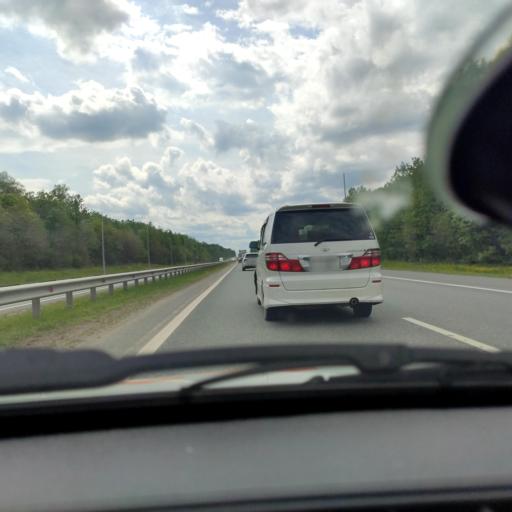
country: RU
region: Bashkortostan
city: Kabakovo
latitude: 54.4149
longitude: 55.9197
